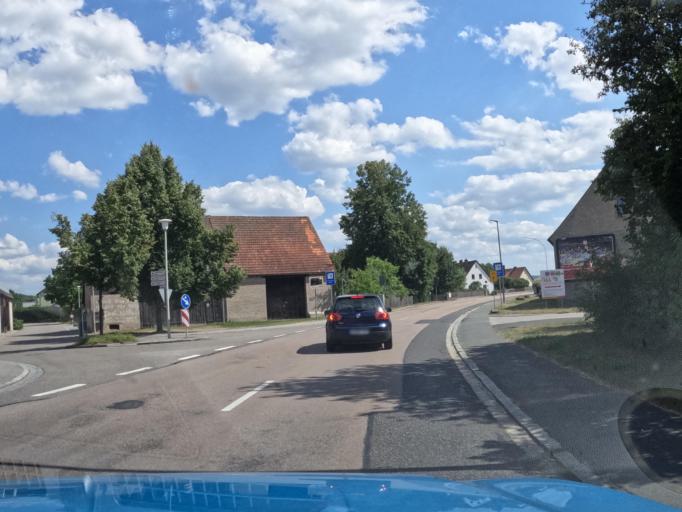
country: DE
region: Bavaria
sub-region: Upper Palatinate
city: Pfreimd
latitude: 49.4915
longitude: 12.1783
